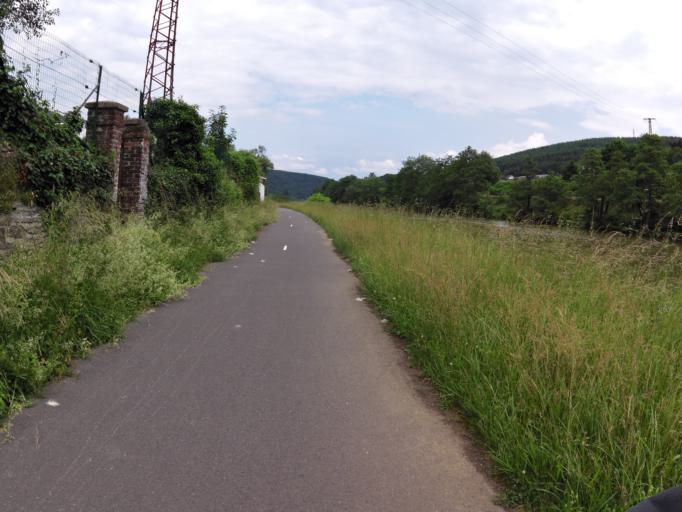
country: FR
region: Champagne-Ardenne
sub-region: Departement des Ardennes
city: Nouzonville
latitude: 49.8196
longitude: 4.7427
